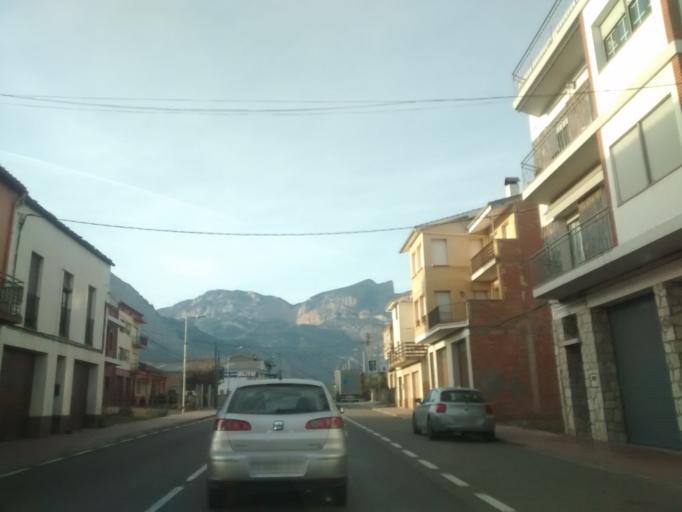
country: ES
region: Catalonia
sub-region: Provincia de Lleida
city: Oliana
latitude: 42.0712
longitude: 1.3112
